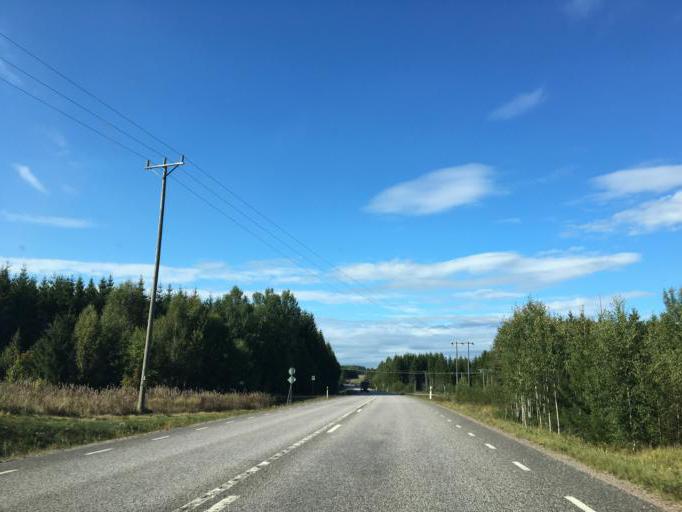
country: SE
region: Soedermanland
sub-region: Nykopings Kommun
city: Nykoping
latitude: 58.8267
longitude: 16.9290
